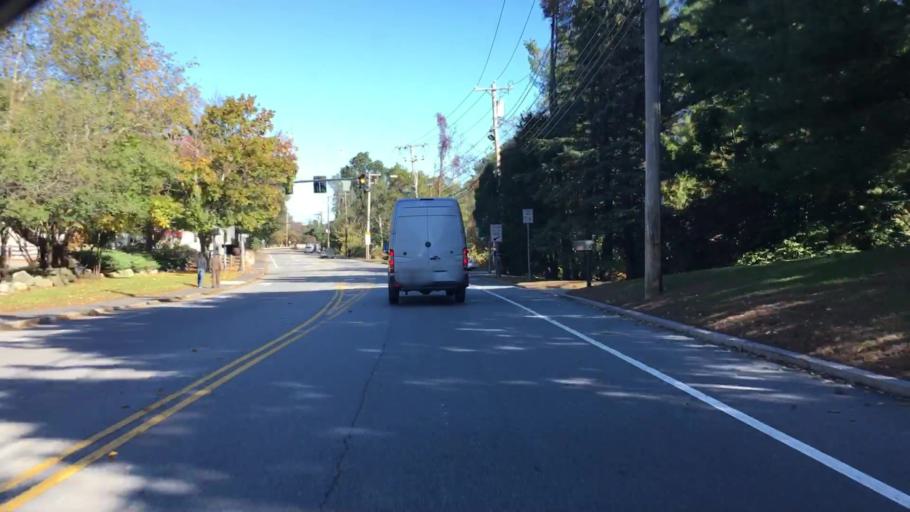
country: US
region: Massachusetts
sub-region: Middlesex County
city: Lexington
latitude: 42.4204
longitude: -71.2513
